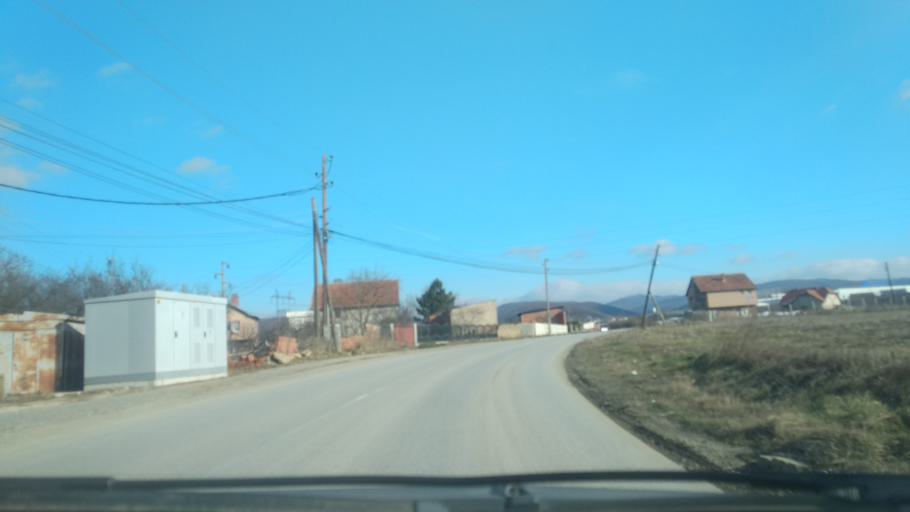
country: XK
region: Pristina
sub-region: Komuna e Prishtines
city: Pristina
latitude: 42.7440
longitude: 21.1280
